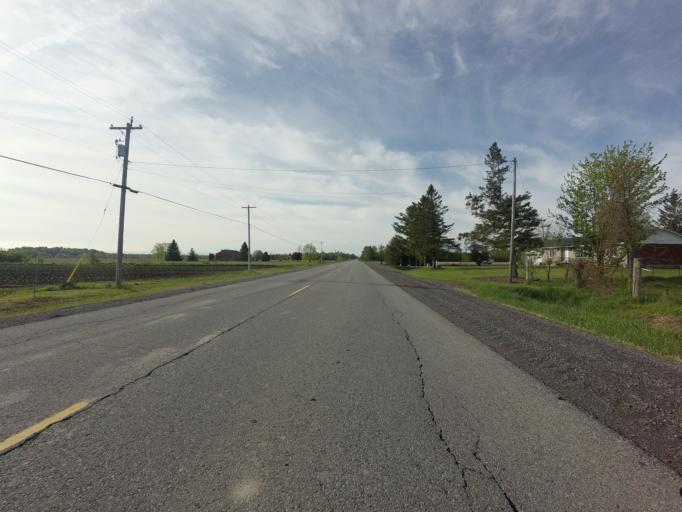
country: CA
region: Ontario
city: Ottawa
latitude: 45.2768
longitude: -75.4412
